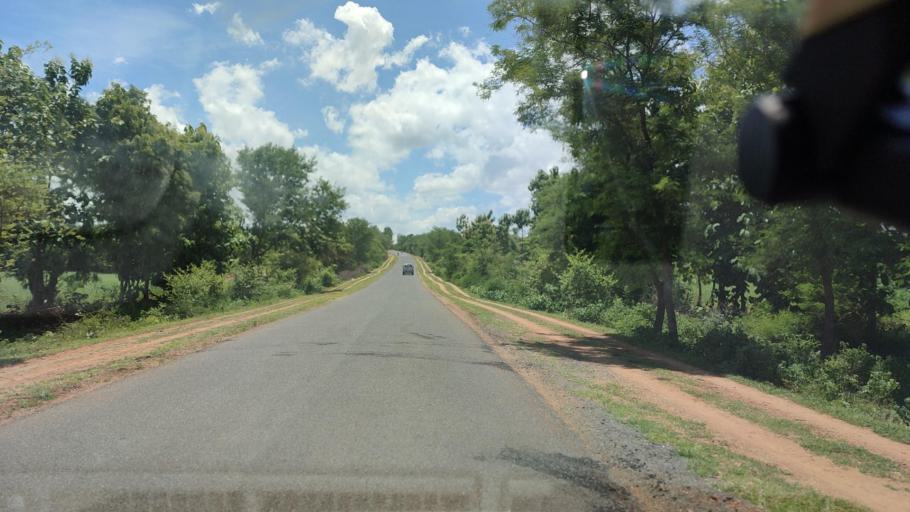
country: MM
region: Magway
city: Magway
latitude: 20.1895
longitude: 95.1879
